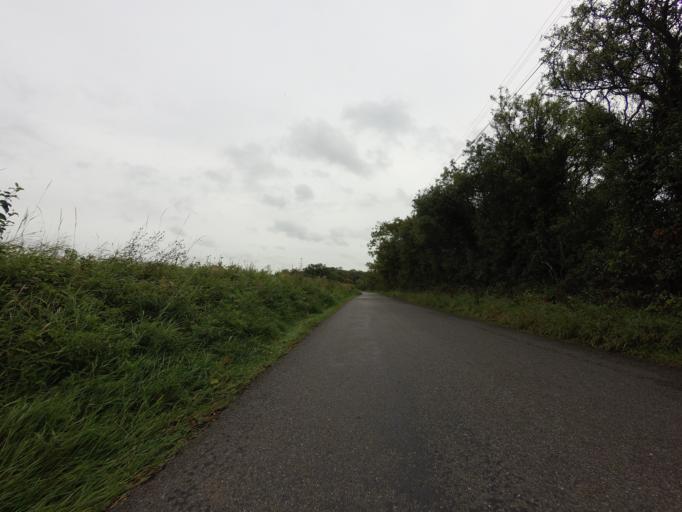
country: GB
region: England
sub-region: Hertfordshire
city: Buntingford
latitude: 51.9721
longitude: 0.0852
